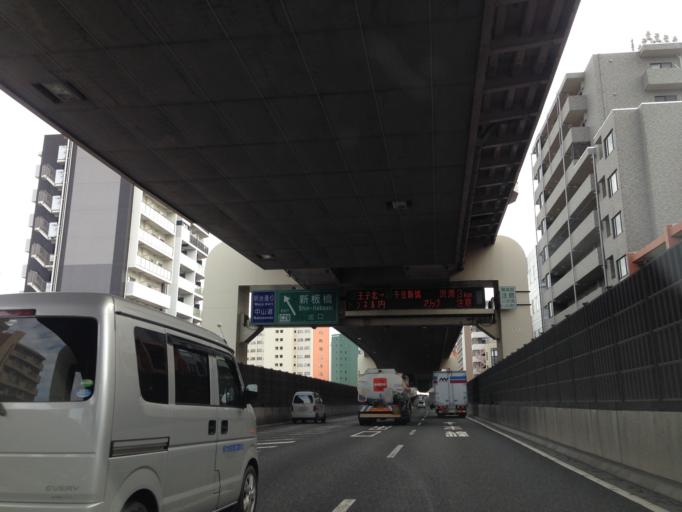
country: JP
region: Saitama
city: Kawaguchi
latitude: 35.7492
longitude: 139.7156
